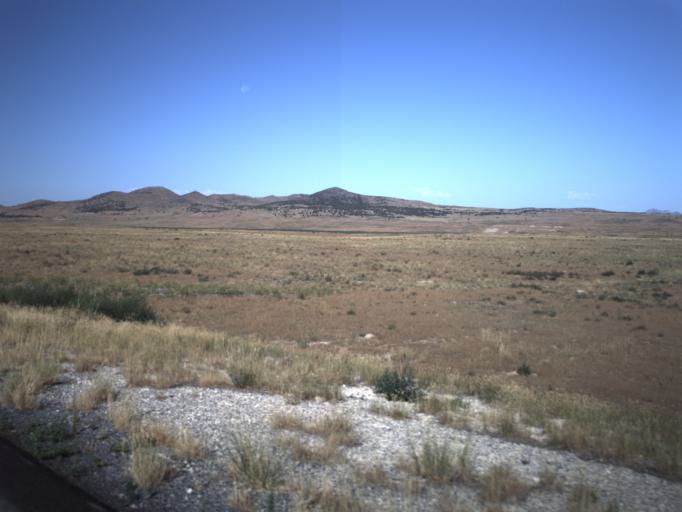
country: US
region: Utah
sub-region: Juab County
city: Mona
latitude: 39.6962
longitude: -112.2271
